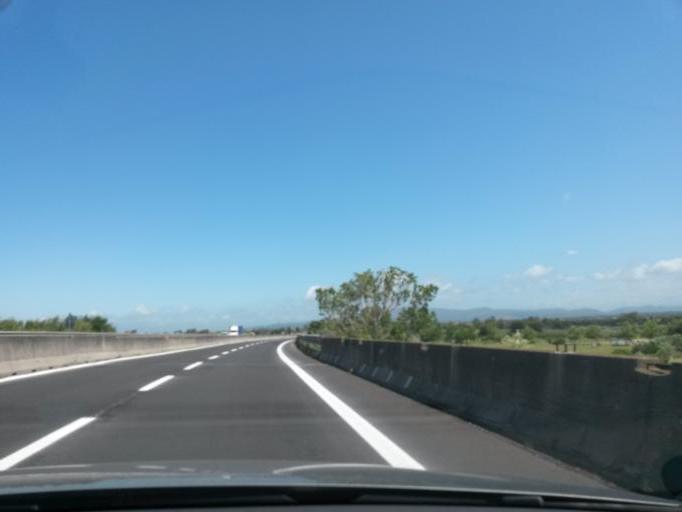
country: IT
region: Tuscany
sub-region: Provincia di Livorno
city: La California
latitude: 43.2751
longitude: 10.5391
